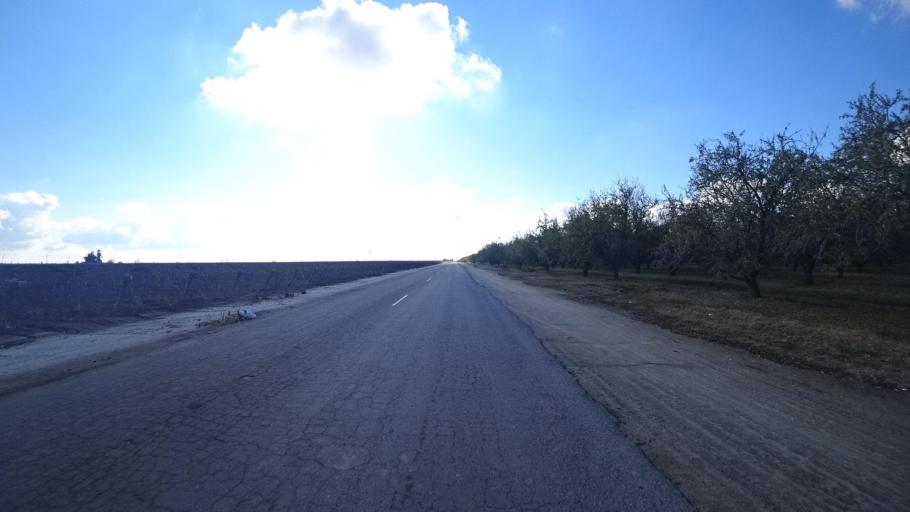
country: US
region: California
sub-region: Kern County
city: McFarland
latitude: 35.6842
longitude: -119.2587
